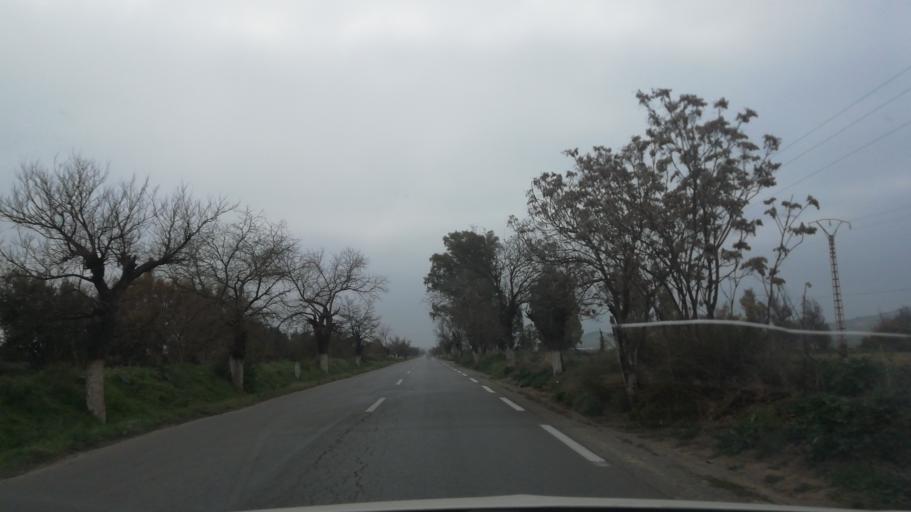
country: DZ
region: Sidi Bel Abbes
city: Sfizef
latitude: 35.2211
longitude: -0.2913
